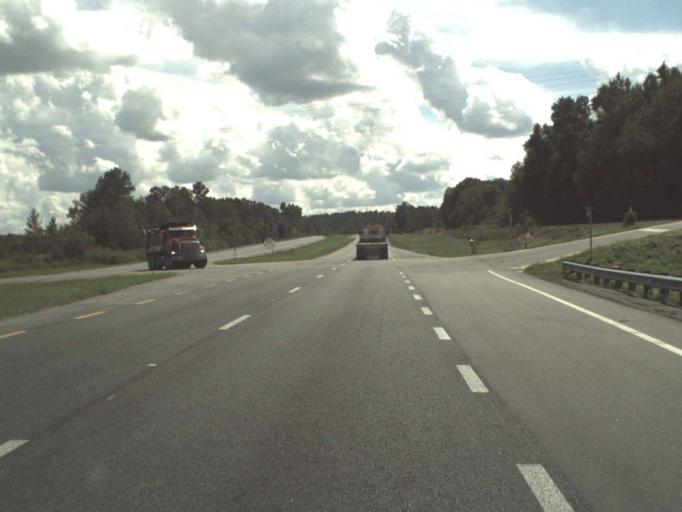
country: US
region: Florida
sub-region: Washington County
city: Chipley
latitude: 30.6683
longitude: -85.3935
